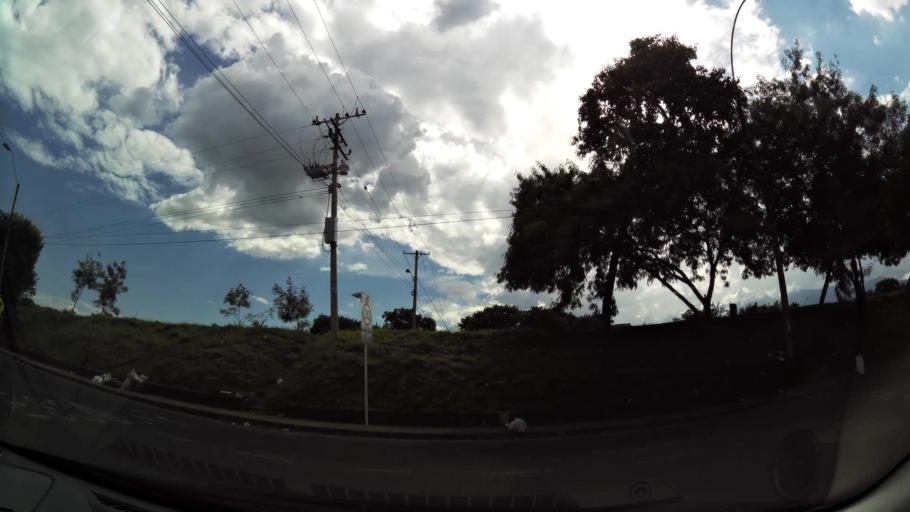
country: CO
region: Valle del Cauca
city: Cali
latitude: 3.3961
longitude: -76.5145
